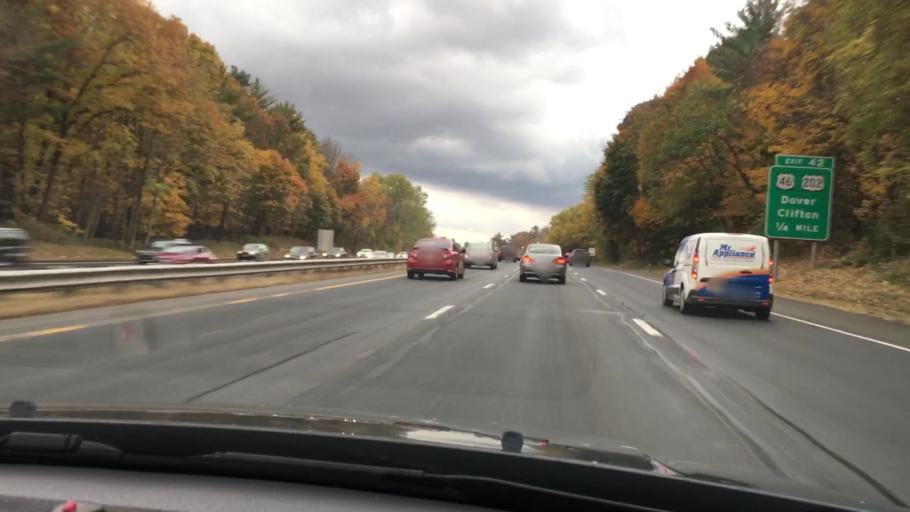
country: US
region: New Jersey
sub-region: Morris County
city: Mountain Lakes
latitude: 40.8807
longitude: -74.4197
